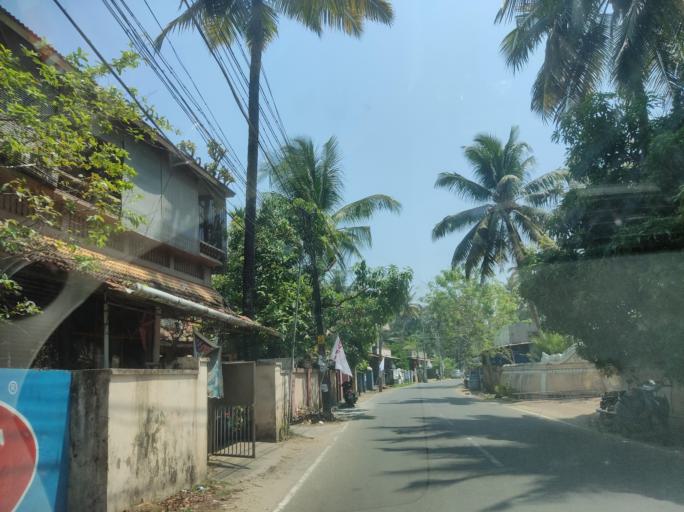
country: IN
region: Kerala
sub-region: Alappuzha
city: Arukutti
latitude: 9.8544
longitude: 76.2938
